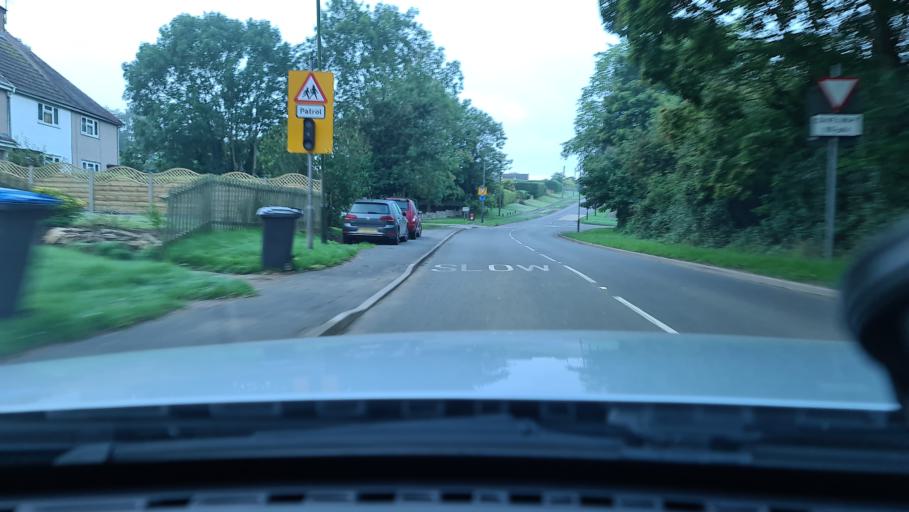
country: GB
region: England
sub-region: Warwickshire
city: Wolston
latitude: 52.3518
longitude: -1.3969
